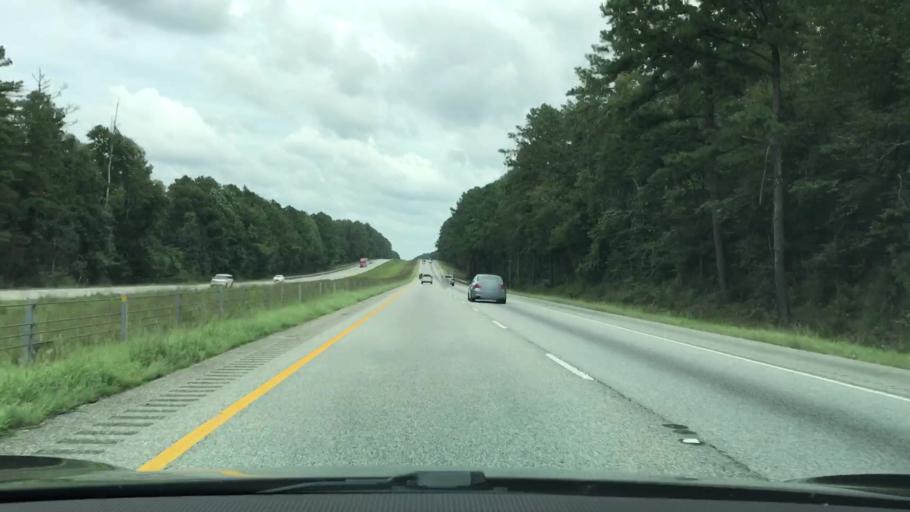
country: US
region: Alabama
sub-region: Chambers County
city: Huguley
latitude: 32.7716
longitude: -85.2577
